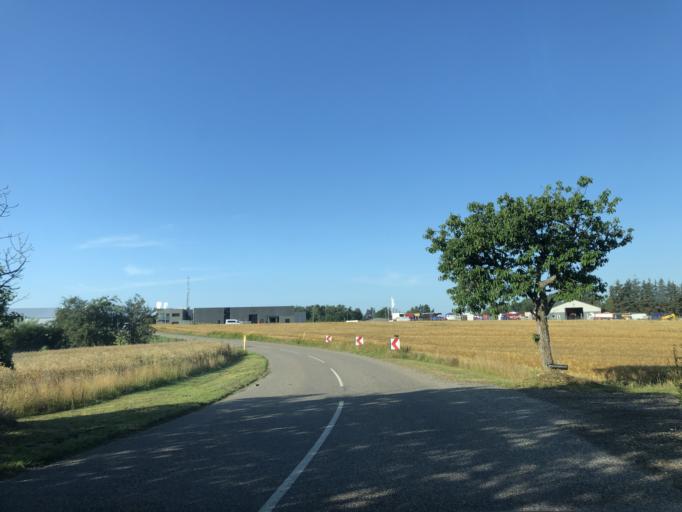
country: DK
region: Central Jutland
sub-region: Silkeborg Kommune
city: Svejbaek
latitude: 56.1599
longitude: 9.6474
